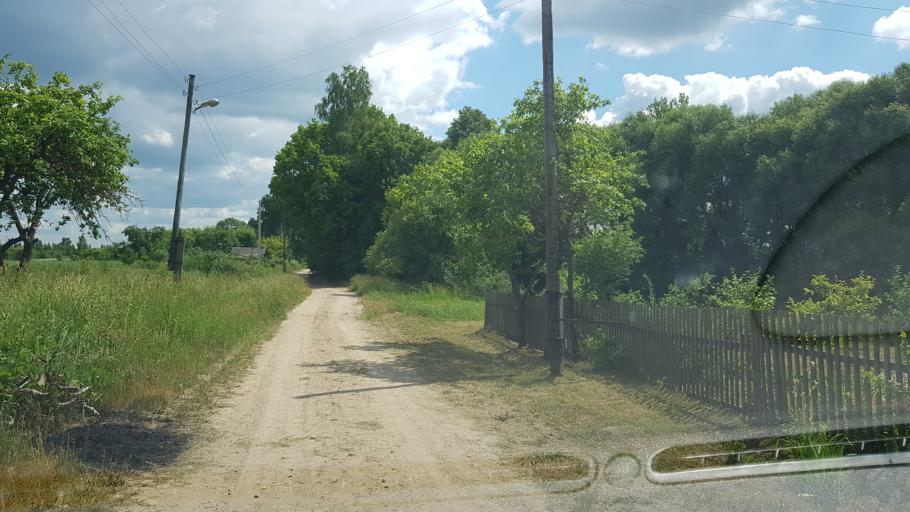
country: BY
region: Vitebsk
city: Dubrowna
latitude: 54.4893
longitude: 30.7997
